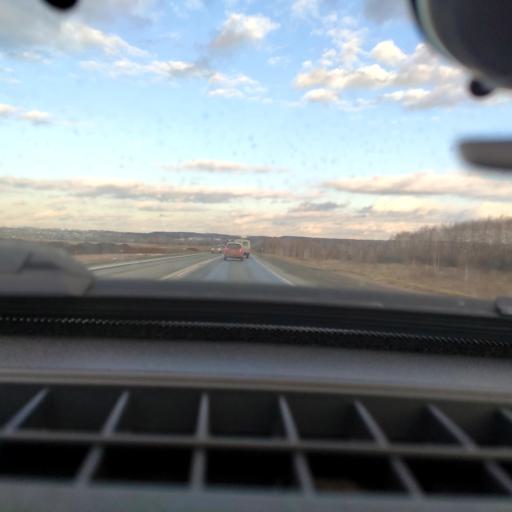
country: RU
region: Bashkortostan
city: Iglino
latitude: 54.7303
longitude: 56.2591
